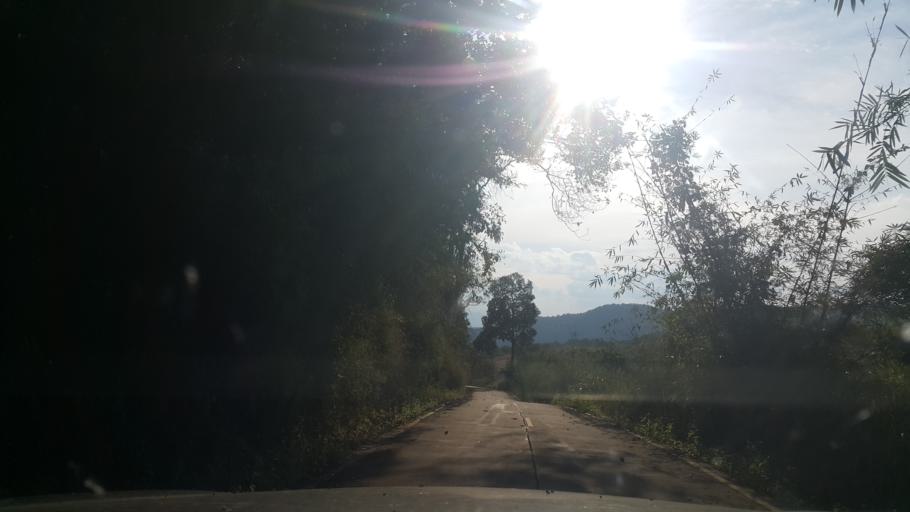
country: TH
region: Chiang Mai
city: Samoeng
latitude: 19.0050
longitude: 98.6882
